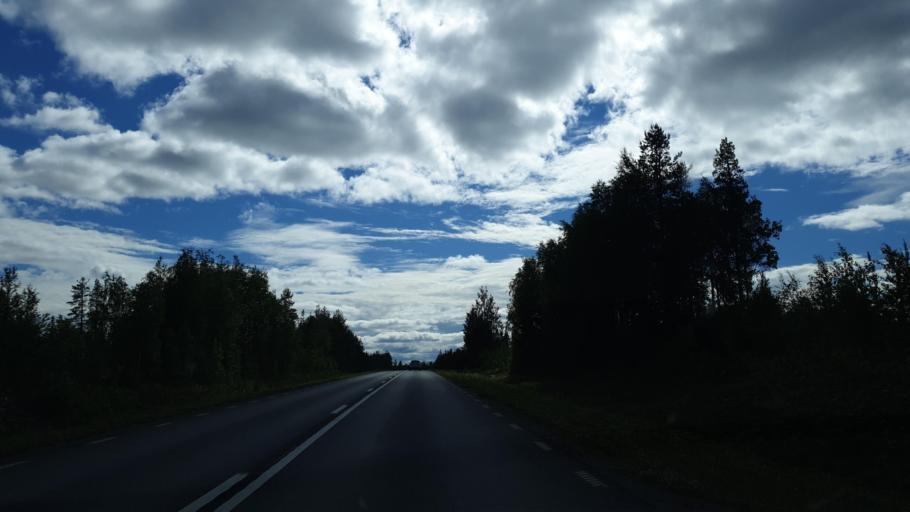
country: SE
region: Vaesterbotten
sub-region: Dorotea Kommun
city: Dorotea
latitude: 64.3239
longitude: 16.6206
